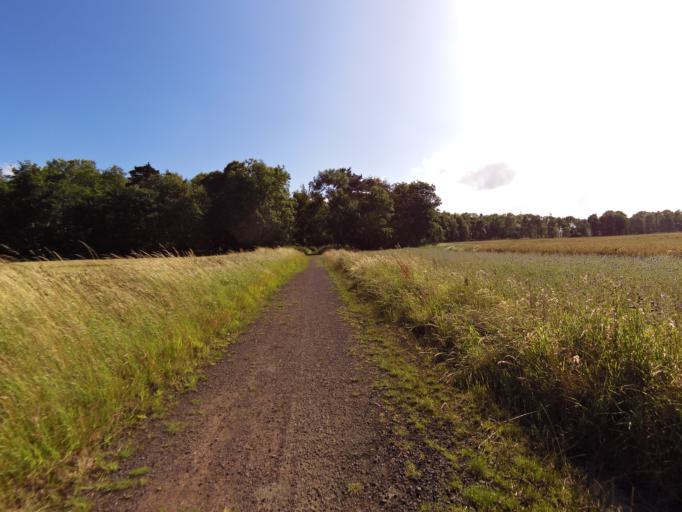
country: GB
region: Scotland
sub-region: East Lothian
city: Gullane
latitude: 56.0427
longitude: -2.7991
